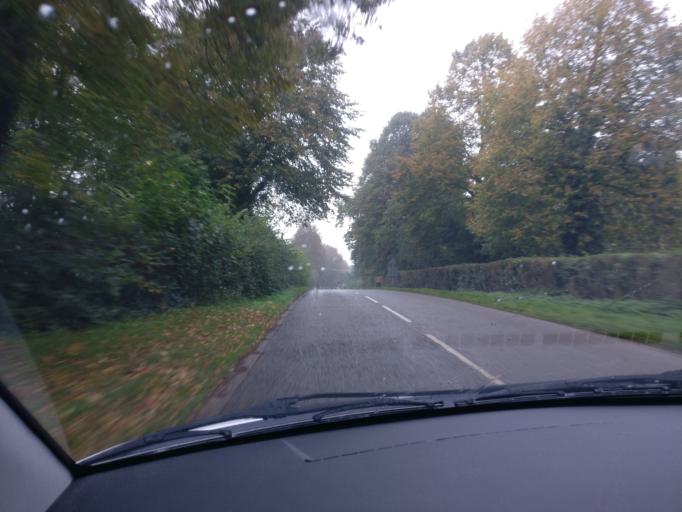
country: GB
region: England
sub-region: Peterborough
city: Castor
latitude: 52.5592
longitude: -0.3043
